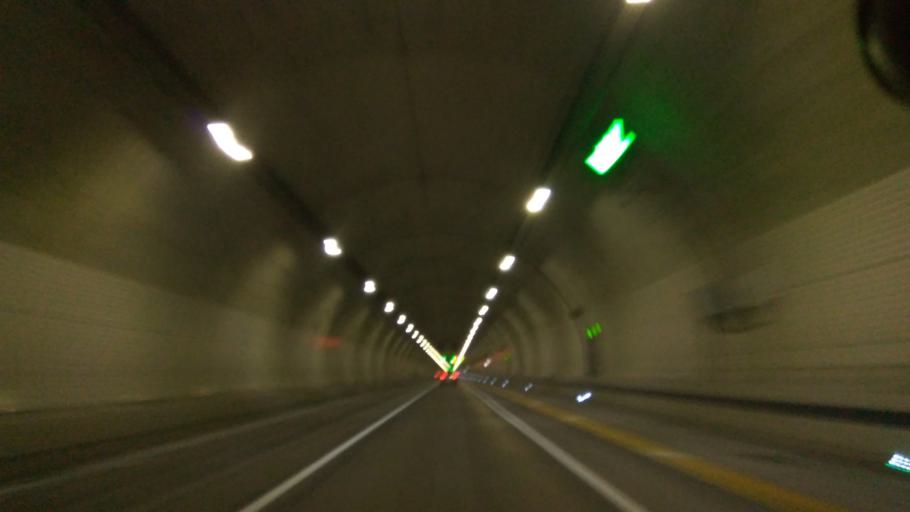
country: KR
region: Gyeonggi-do
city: Cheongpyeong
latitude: 37.6501
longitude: 127.4624
